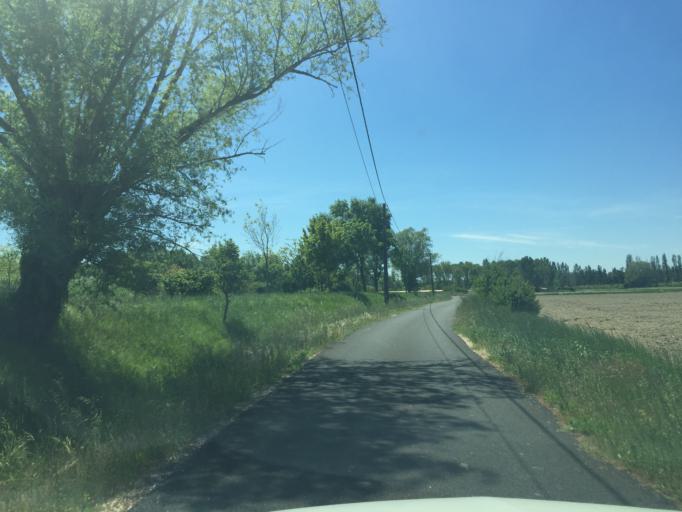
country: FR
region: Provence-Alpes-Cote d'Azur
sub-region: Departement du Vaucluse
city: Caderousse
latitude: 44.0981
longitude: 4.7877
